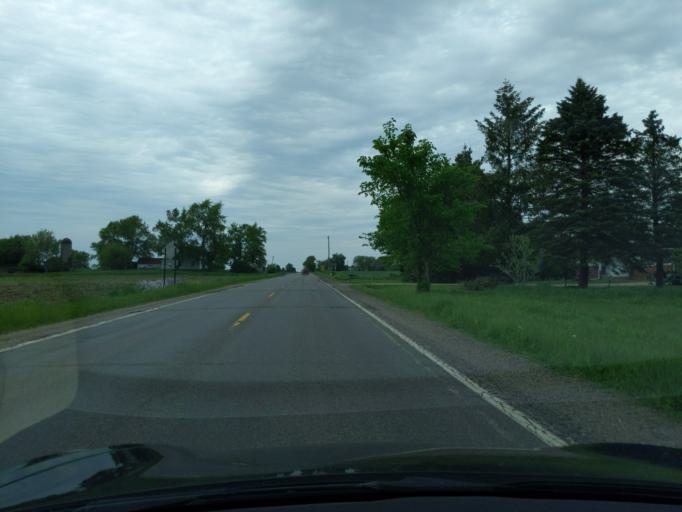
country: US
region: Michigan
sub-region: Ingham County
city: Mason
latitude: 42.6261
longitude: -84.3639
